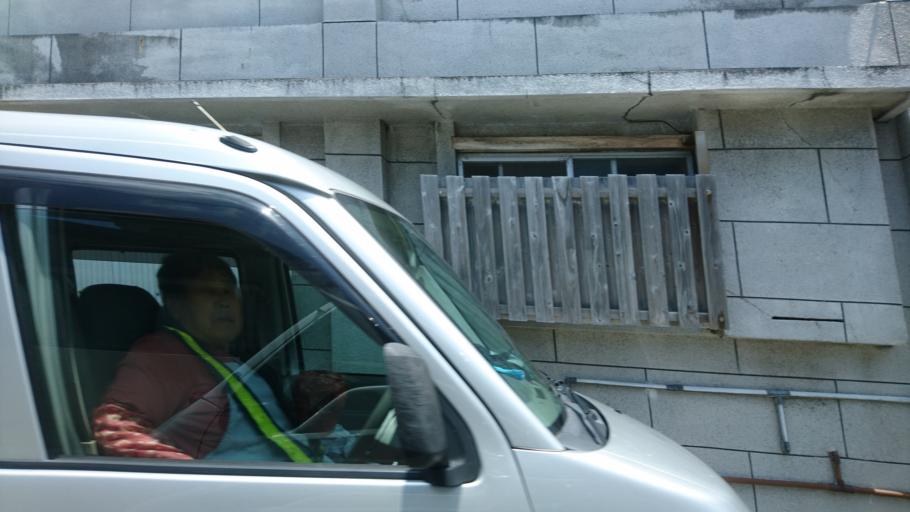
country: JP
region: Shizuoka
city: Shimoda
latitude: 34.4211
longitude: 139.2826
